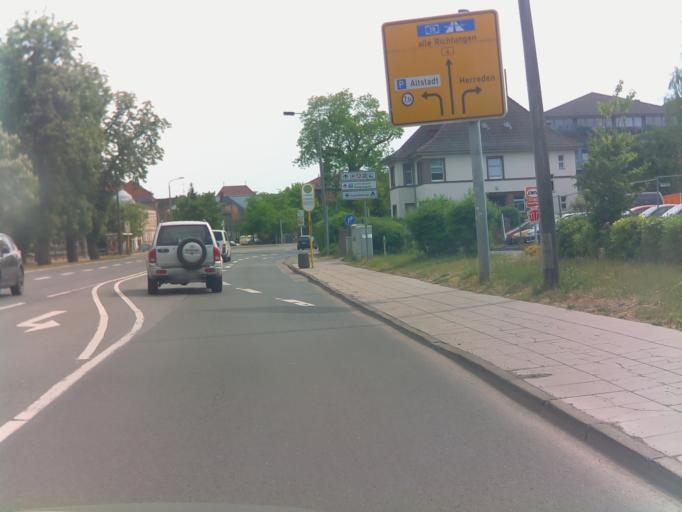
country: DE
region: Thuringia
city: Nordhausen
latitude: 51.5107
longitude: 10.7855
